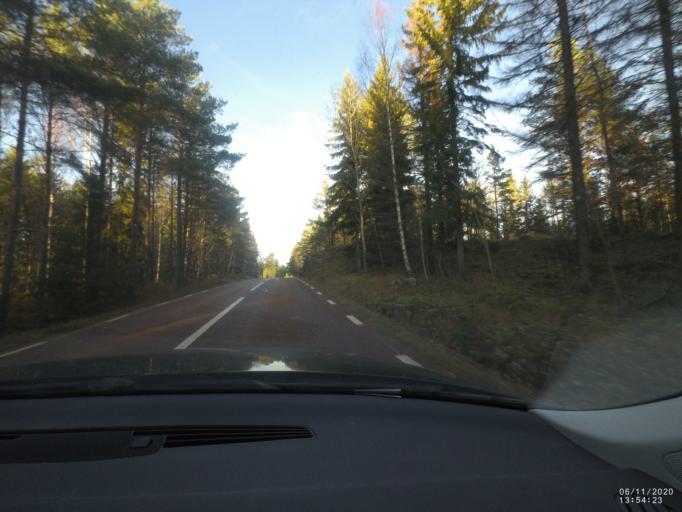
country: SE
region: Soedermanland
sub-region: Gnesta Kommun
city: Gnesta
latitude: 58.9699
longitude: 17.1463
